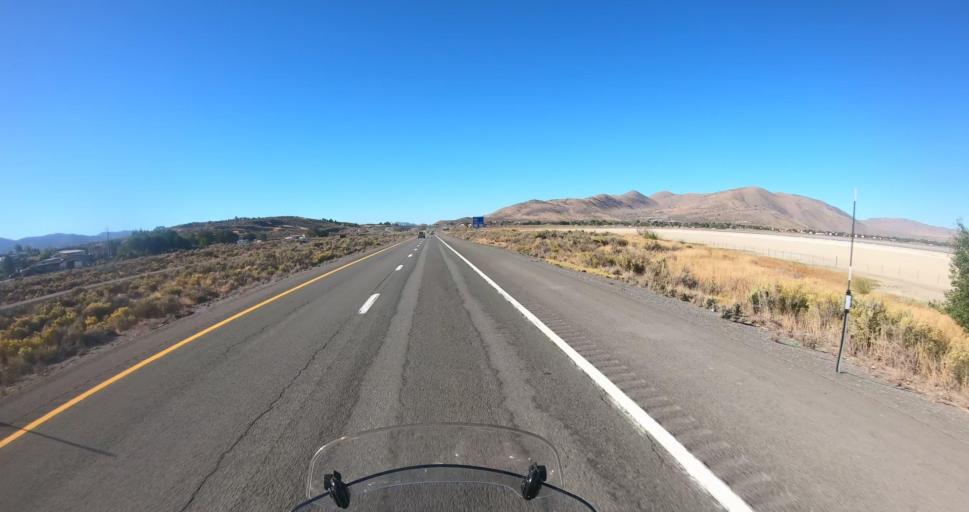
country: US
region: Nevada
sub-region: Washoe County
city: Cold Springs
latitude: 39.6594
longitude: -119.9888
